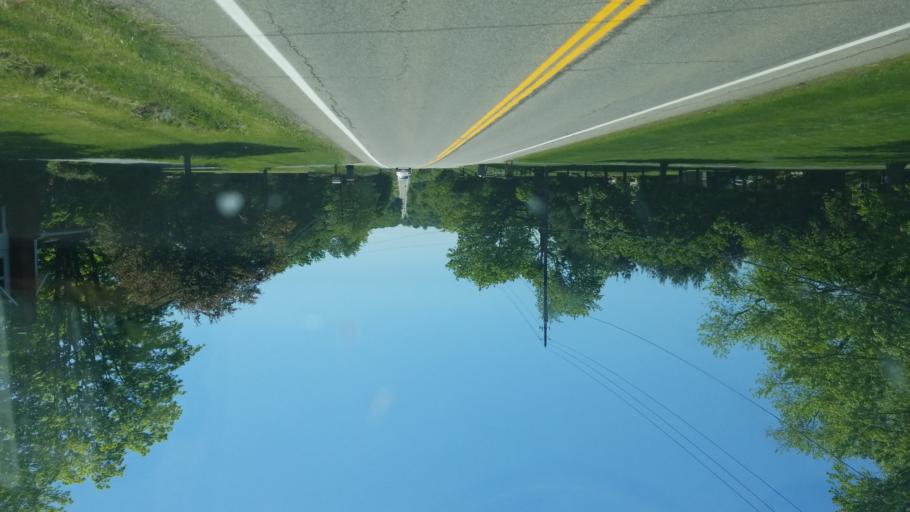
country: US
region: Ohio
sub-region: Geauga County
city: Burton
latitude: 41.4708
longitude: -81.1702
